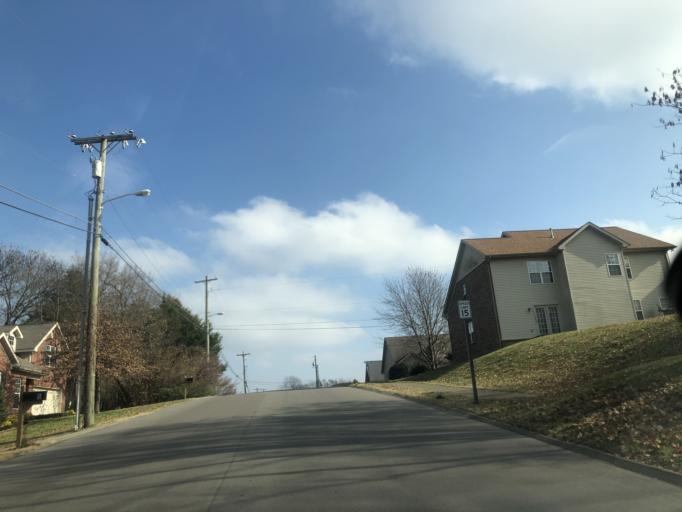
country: US
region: Tennessee
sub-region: Davidson County
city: Oak Hill
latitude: 36.1040
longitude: -86.7206
